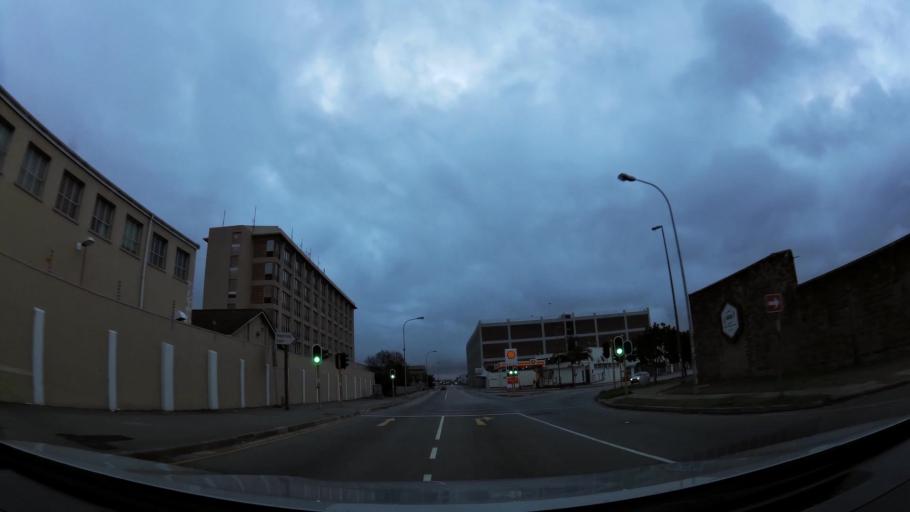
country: ZA
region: Eastern Cape
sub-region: Nelson Mandela Bay Metropolitan Municipality
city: Port Elizabeth
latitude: -33.9454
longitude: 25.6032
